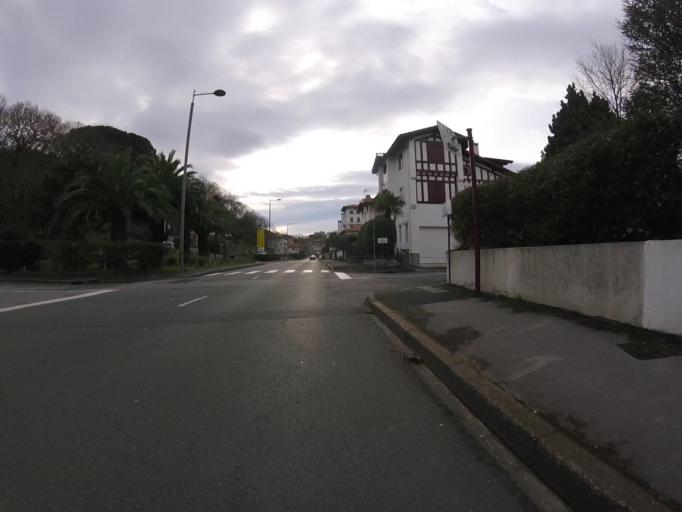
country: FR
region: Aquitaine
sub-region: Departement des Pyrenees-Atlantiques
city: Hendaye
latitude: 43.3688
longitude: -1.7712
